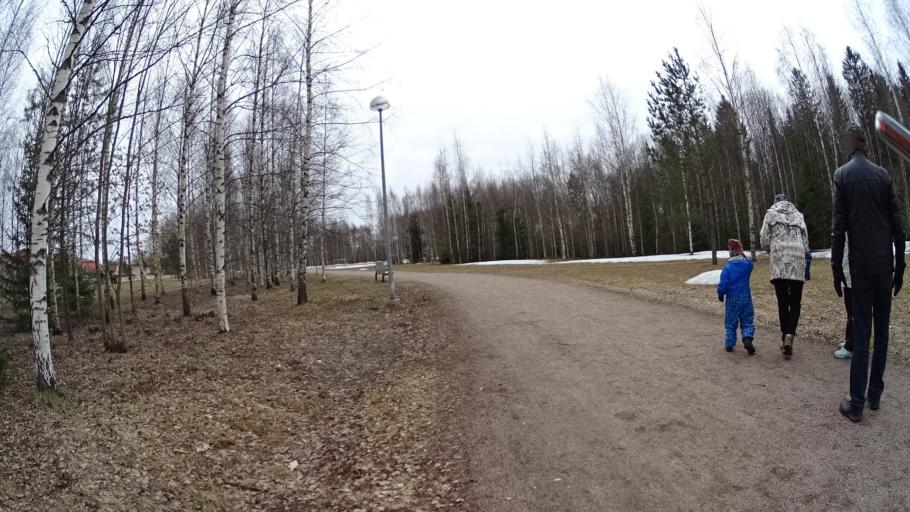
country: FI
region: Uusimaa
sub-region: Helsinki
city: Vantaa
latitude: 60.2879
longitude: 24.9395
